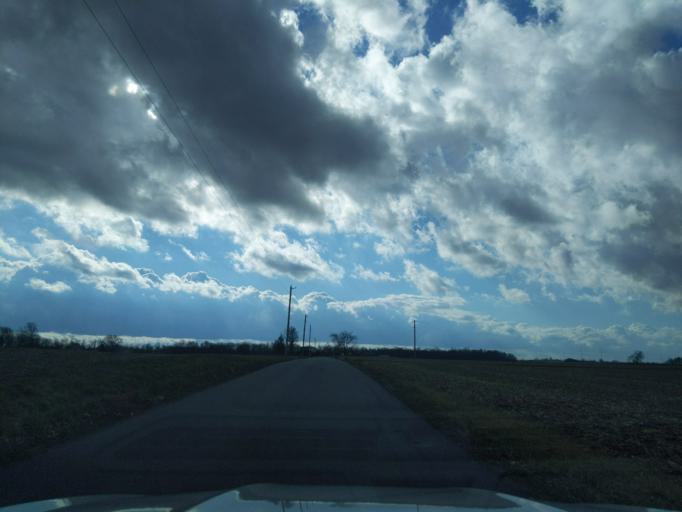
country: US
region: Indiana
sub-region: Decatur County
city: Greensburg
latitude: 39.3763
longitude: -85.5034
